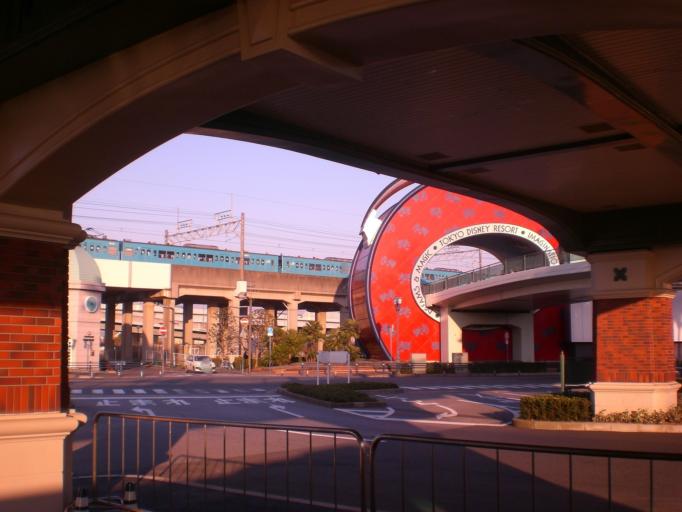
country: JP
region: Tokyo
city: Urayasu
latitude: 35.6365
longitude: 139.8810
